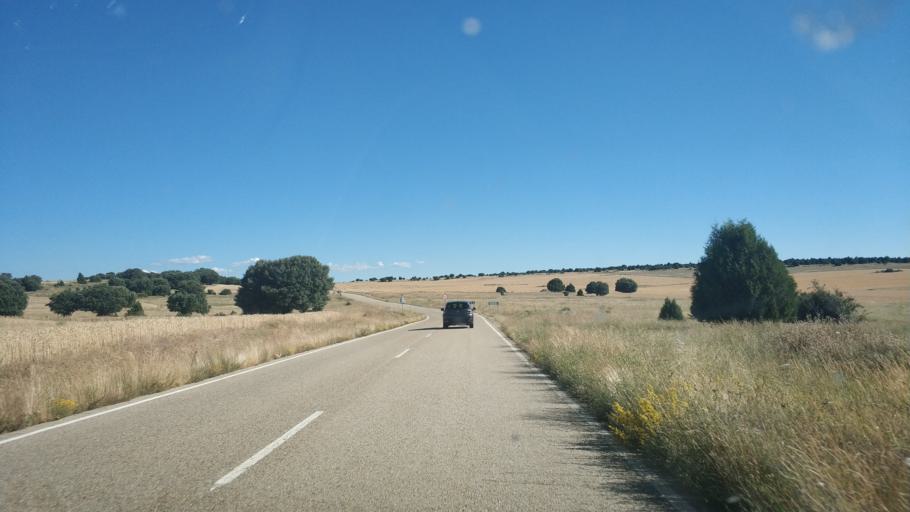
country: ES
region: Castille and Leon
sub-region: Provincia de Soria
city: Montejo de Tiermes
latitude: 41.3977
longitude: -3.1993
